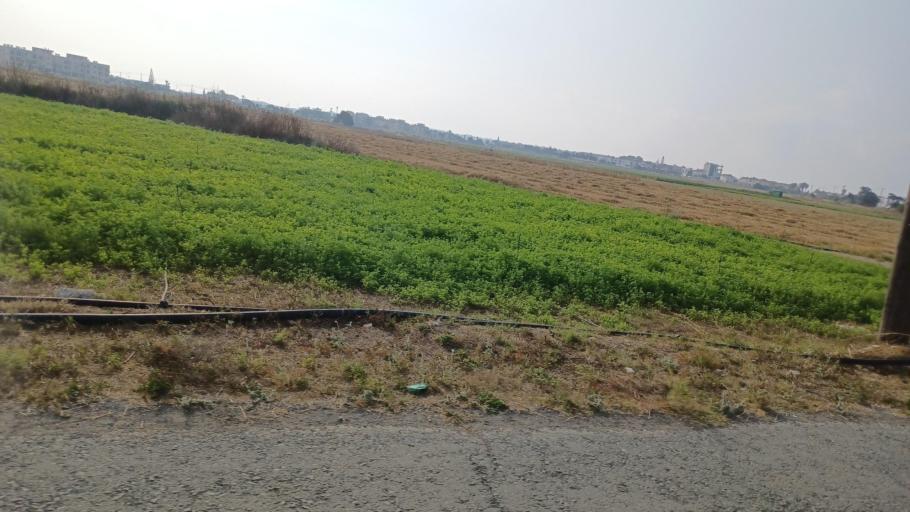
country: CY
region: Larnaka
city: Perivolia
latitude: 34.8248
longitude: 33.5781
